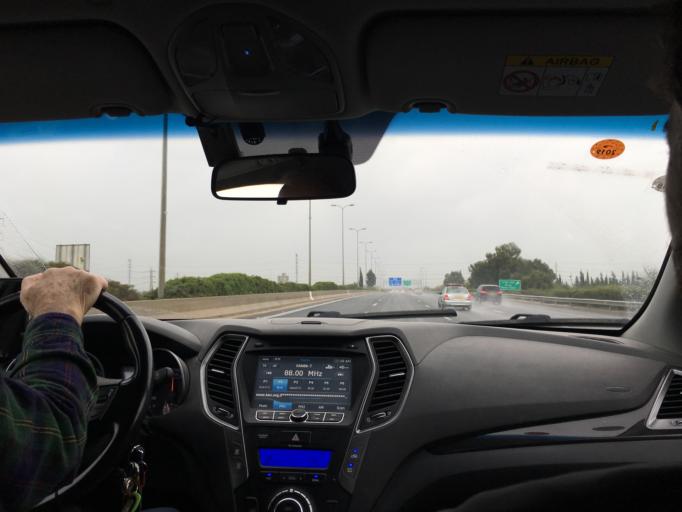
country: IL
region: Central District
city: Petah Tiqwa
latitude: 32.1198
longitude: 34.8697
